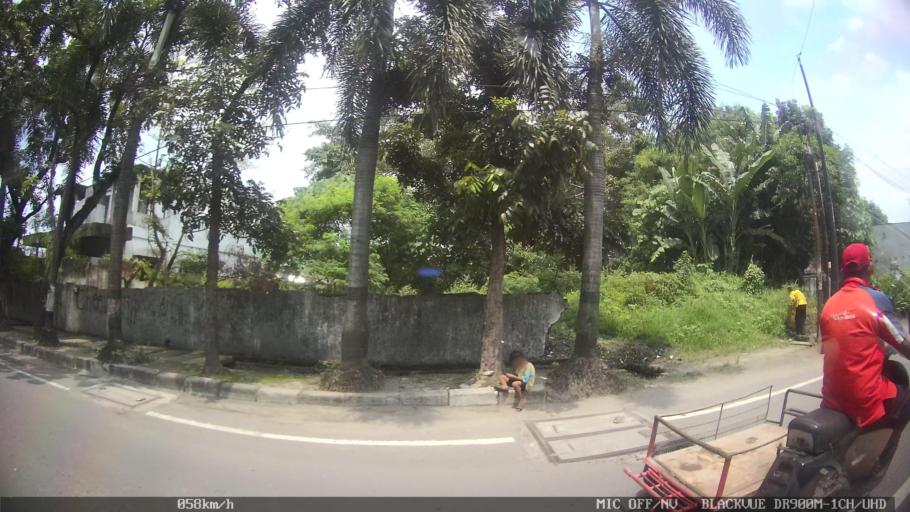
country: ID
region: North Sumatra
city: Medan
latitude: 3.6401
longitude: 98.6637
